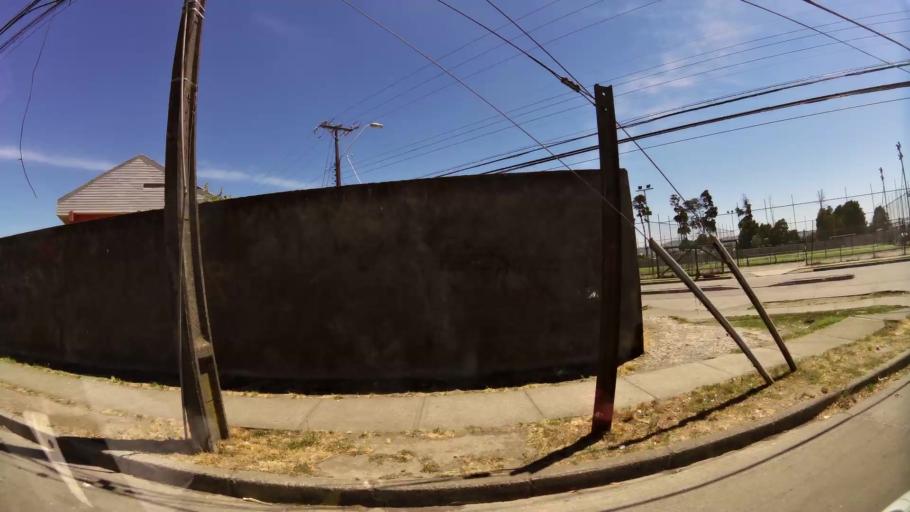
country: CL
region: Biobio
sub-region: Provincia de Concepcion
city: Talcahuano
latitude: -36.7462
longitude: -73.0899
